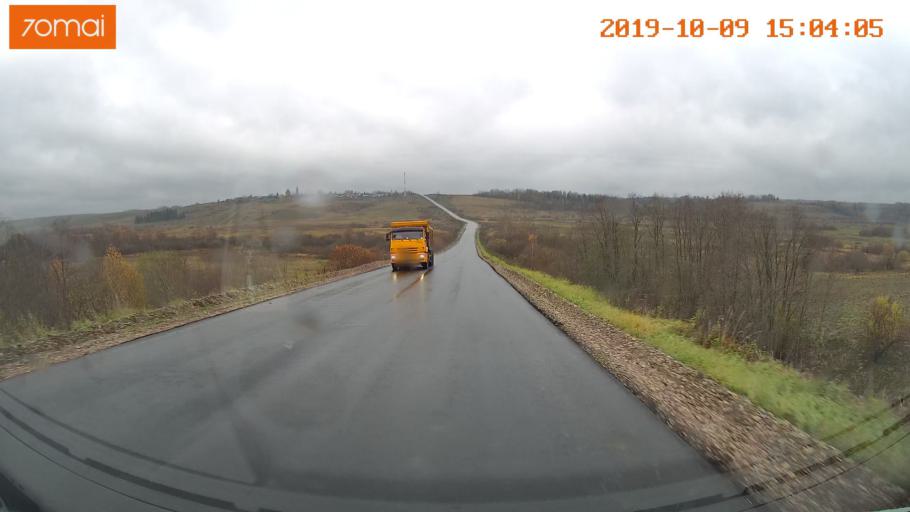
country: RU
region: Kostroma
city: Chistyye Bory
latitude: 58.2630
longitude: 41.6704
